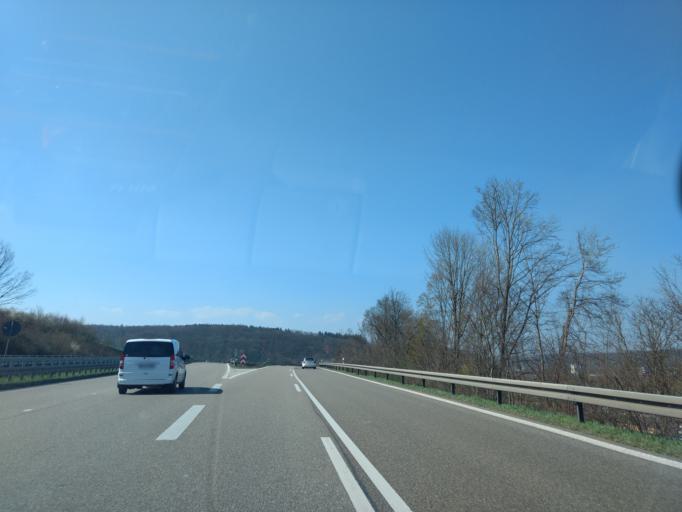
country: DE
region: Baden-Wuerttemberg
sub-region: Regierungsbezirk Stuttgart
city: Plochingen
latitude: 48.7027
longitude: 9.4249
